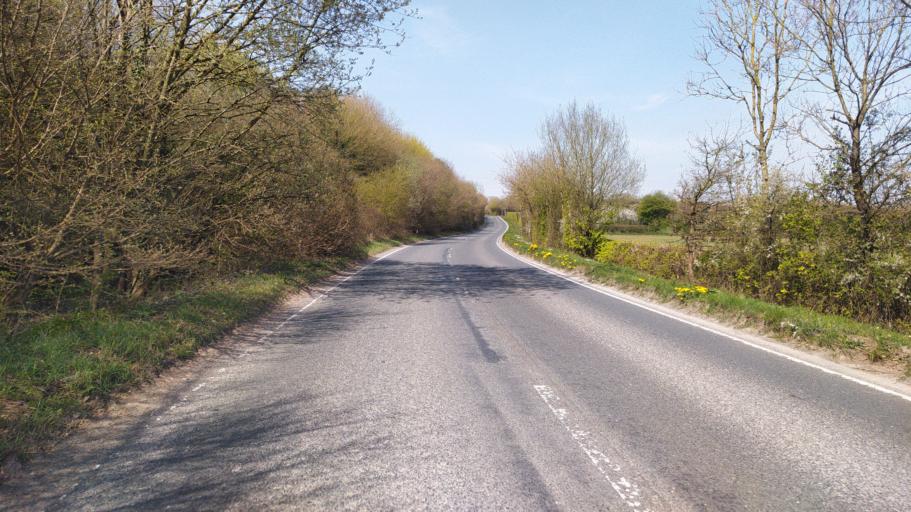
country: GB
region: England
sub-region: Somerset
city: Frome
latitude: 51.2123
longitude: -2.3915
